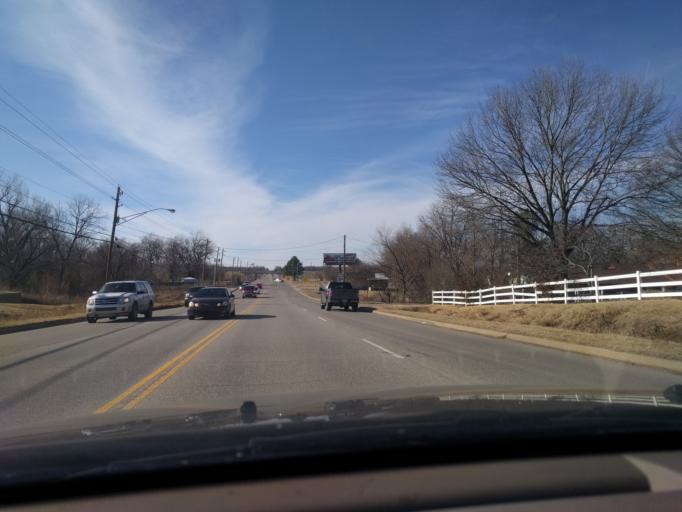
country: US
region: Oklahoma
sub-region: Tulsa County
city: Broken Arrow
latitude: 36.0609
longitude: -95.7331
